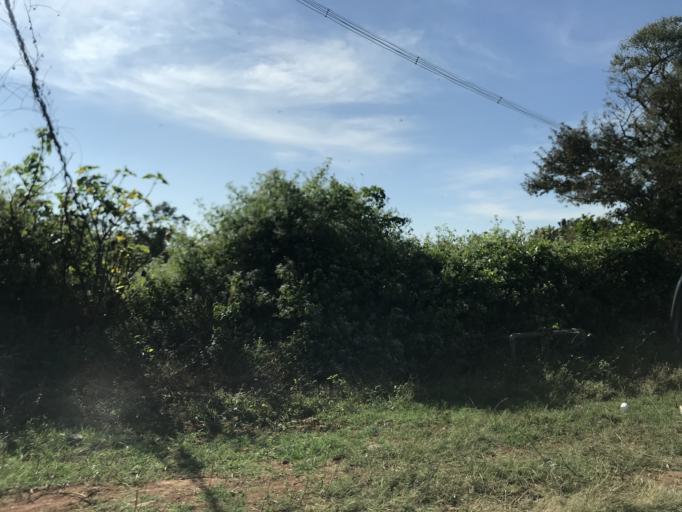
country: IN
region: Karnataka
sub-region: Mysore
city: Mysore
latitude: 12.1965
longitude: 76.5460
